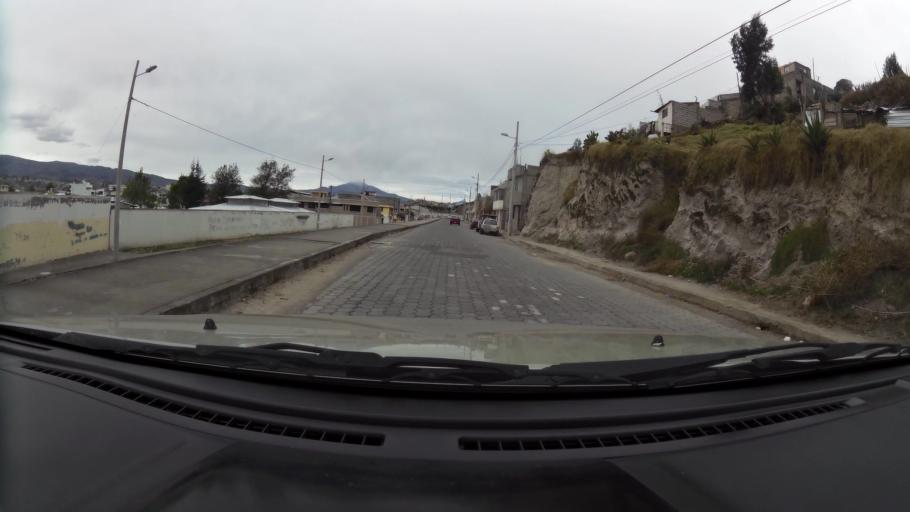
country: EC
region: Cotopaxi
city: Latacunga
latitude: -0.9367
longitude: -78.6140
